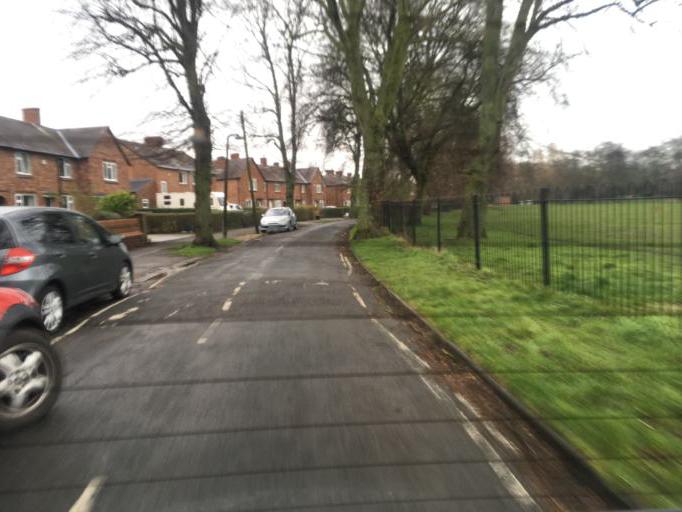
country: GB
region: England
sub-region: City of York
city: Heslington
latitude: 53.9609
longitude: -1.0596
